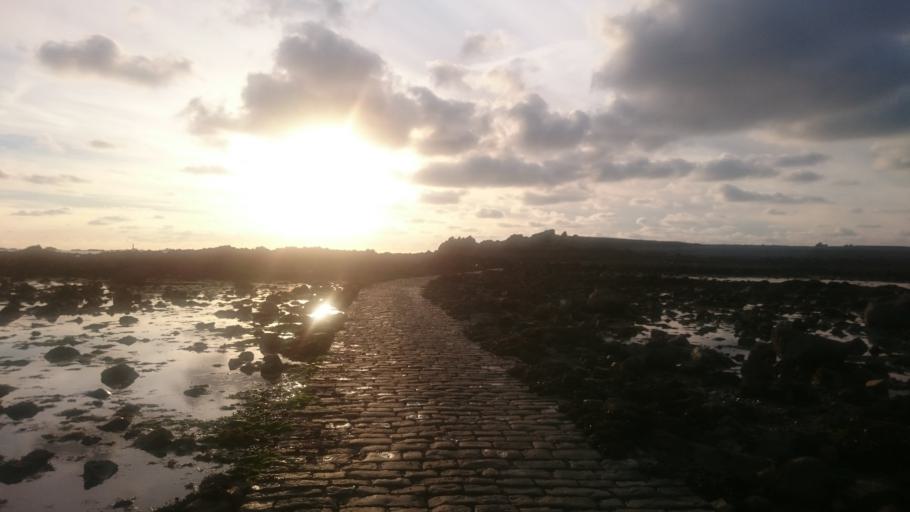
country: GG
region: St Peter Port
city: Saint Peter Port
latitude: 49.4585
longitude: -2.6597
